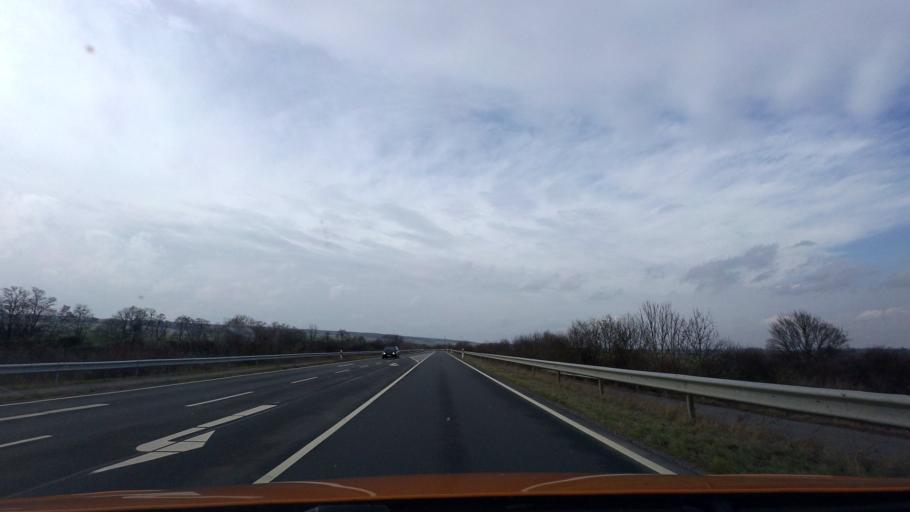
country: DE
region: Lower Saxony
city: Rabke
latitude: 52.2305
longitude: 10.8645
